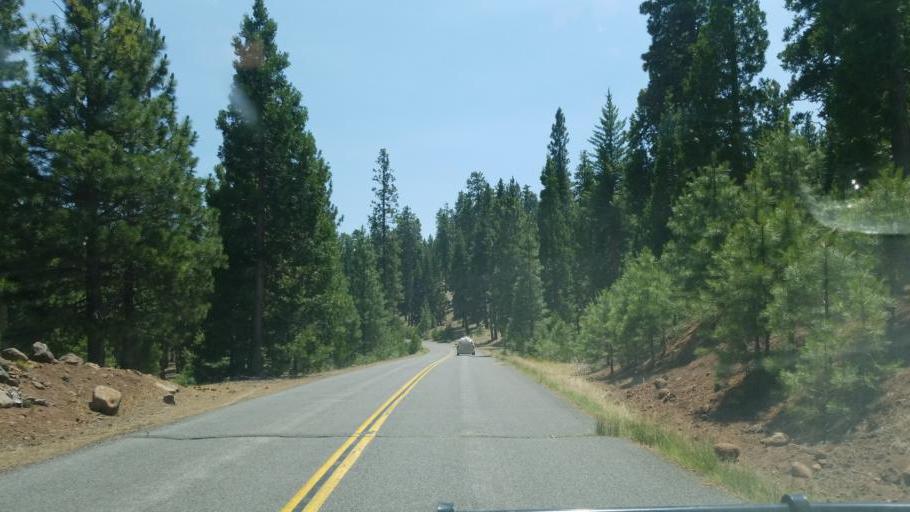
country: US
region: California
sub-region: Lassen County
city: Susanville
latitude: 40.5578
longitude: -120.8267
